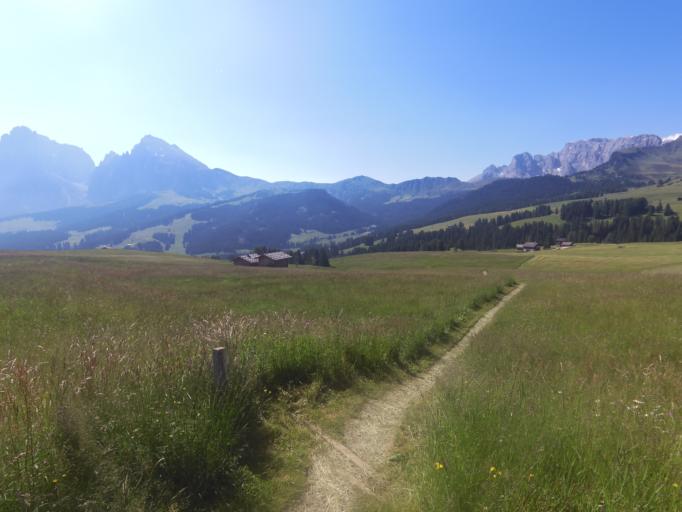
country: IT
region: Trentino-Alto Adige
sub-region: Bolzano
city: Ortisei
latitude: 46.5374
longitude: 11.6546
